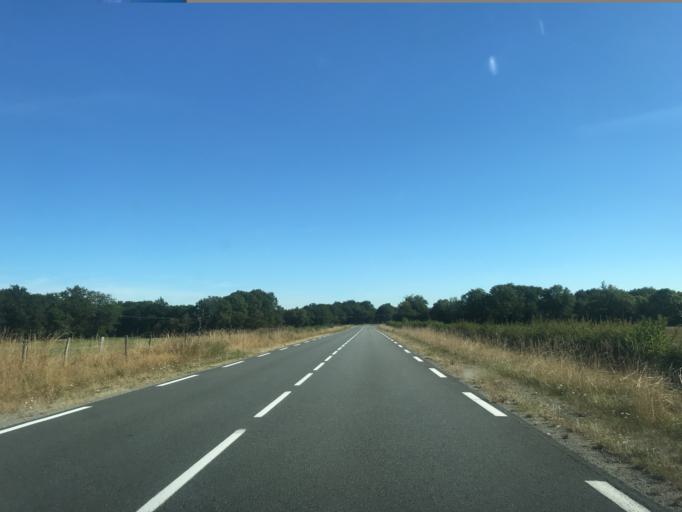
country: FR
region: Limousin
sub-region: Departement de la Creuse
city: Gouzon
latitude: 46.1765
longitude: 2.2245
